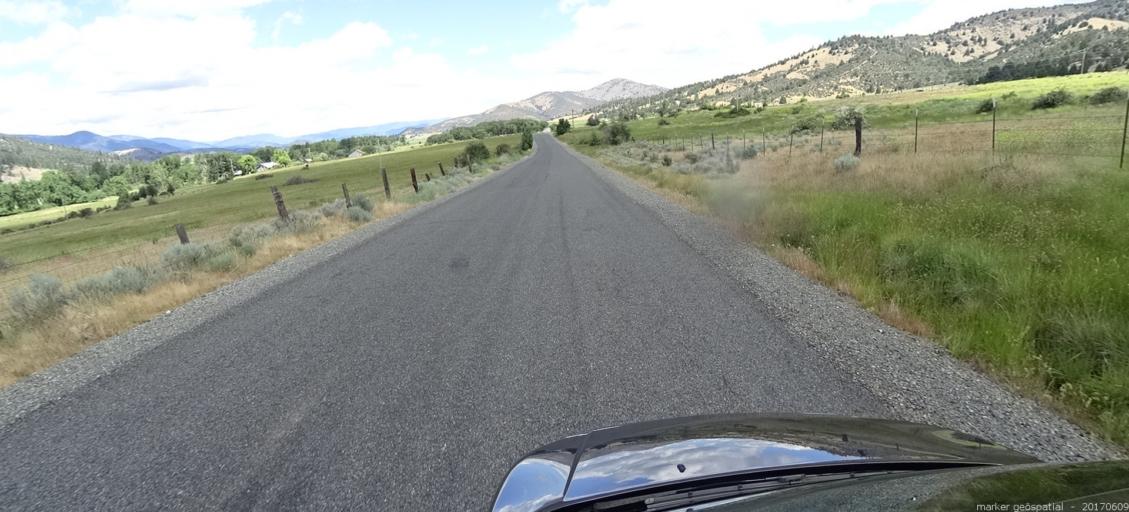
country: US
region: California
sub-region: Siskiyou County
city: Yreka
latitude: 41.3721
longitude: -122.8224
